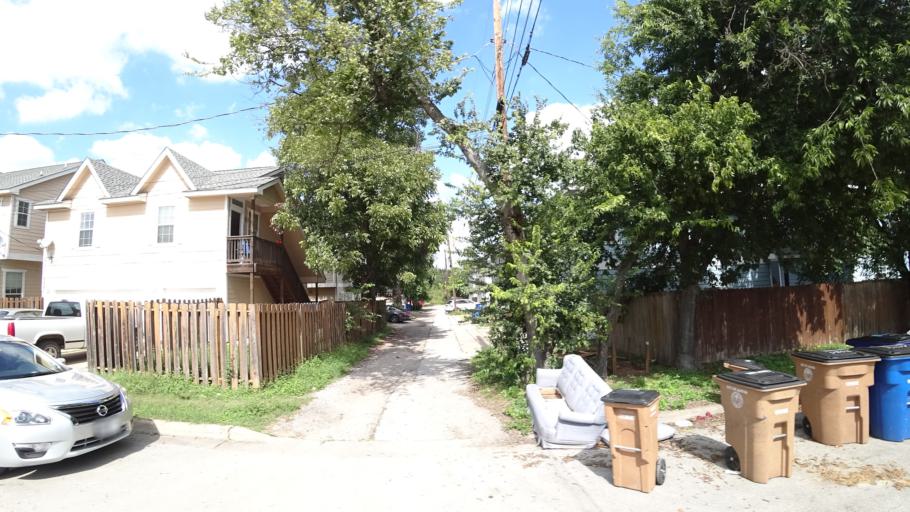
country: US
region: Texas
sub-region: Travis County
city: Austin
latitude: 30.3168
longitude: -97.7164
